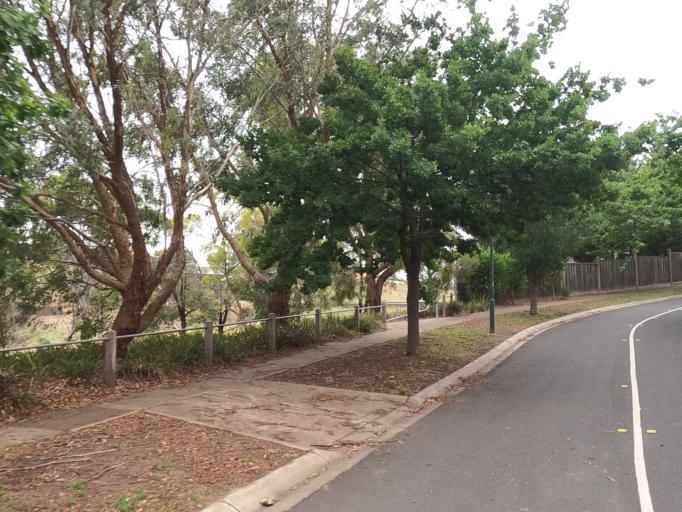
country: AU
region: Victoria
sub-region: Hume
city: Meadow Heights
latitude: -37.6539
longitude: 144.9053
